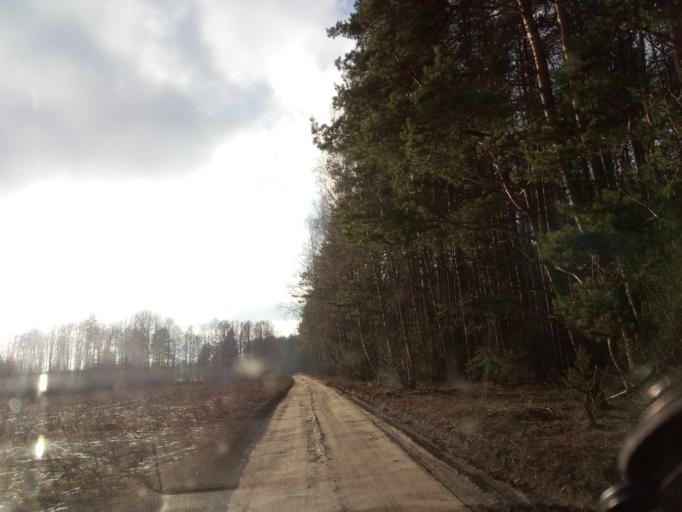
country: LT
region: Alytaus apskritis
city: Druskininkai
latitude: 53.9451
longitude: 24.2816
